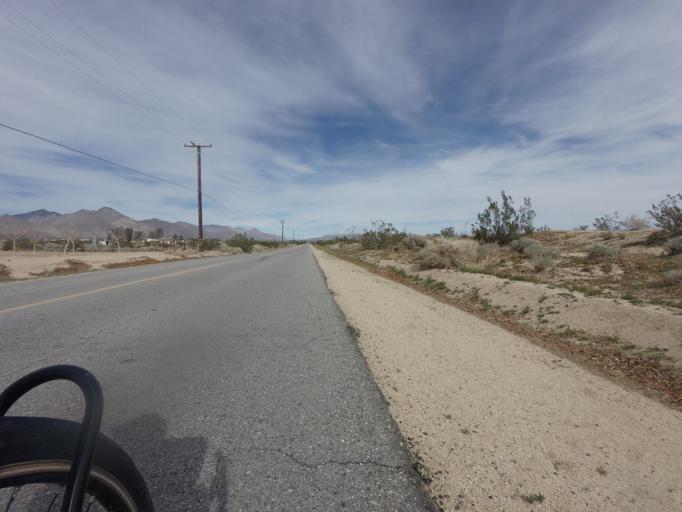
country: US
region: California
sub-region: Kern County
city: Inyokern
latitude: 35.7306
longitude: -117.8371
